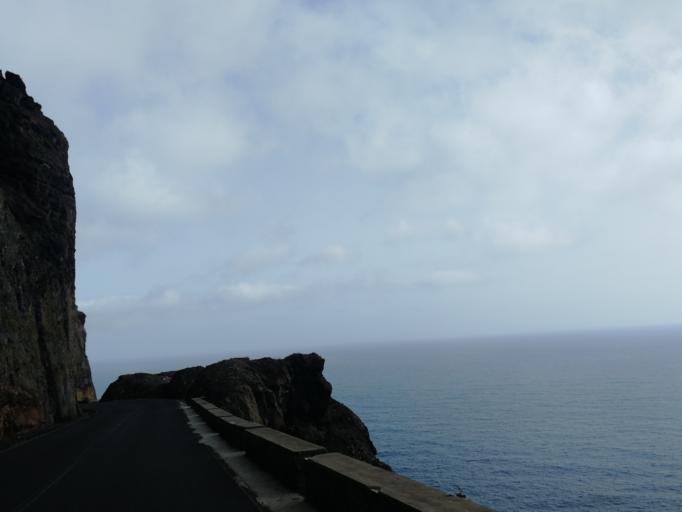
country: CV
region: Paul
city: Pombas
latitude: 17.1128
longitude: -24.9763
